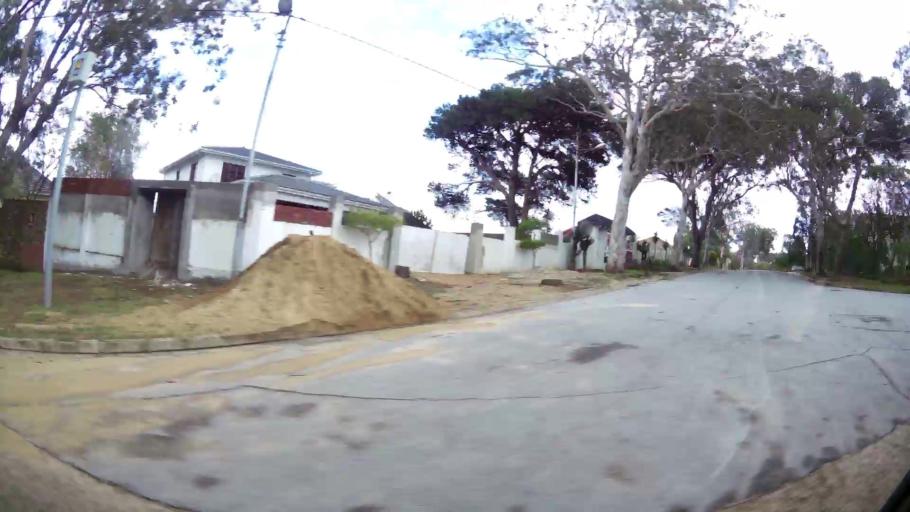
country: ZA
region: Eastern Cape
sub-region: Nelson Mandela Bay Metropolitan Municipality
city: Port Elizabeth
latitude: -33.9665
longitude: 25.5903
